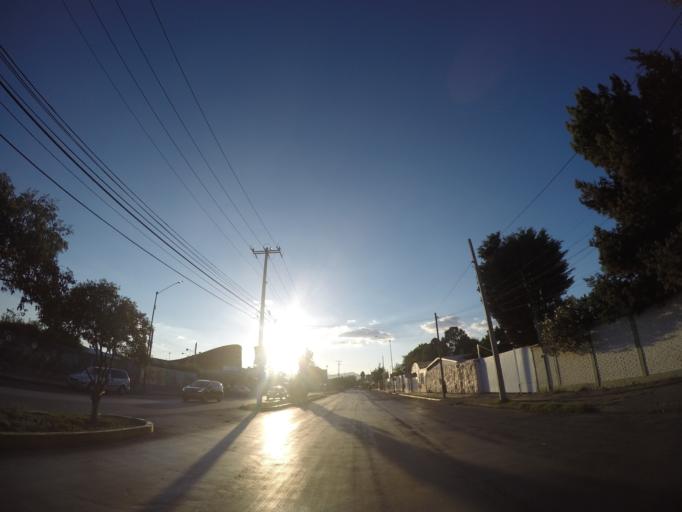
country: MX
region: San Luis Potosi
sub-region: San Luis Potosi
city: San Luis Potosi
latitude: 22.1373
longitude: -100.9851
